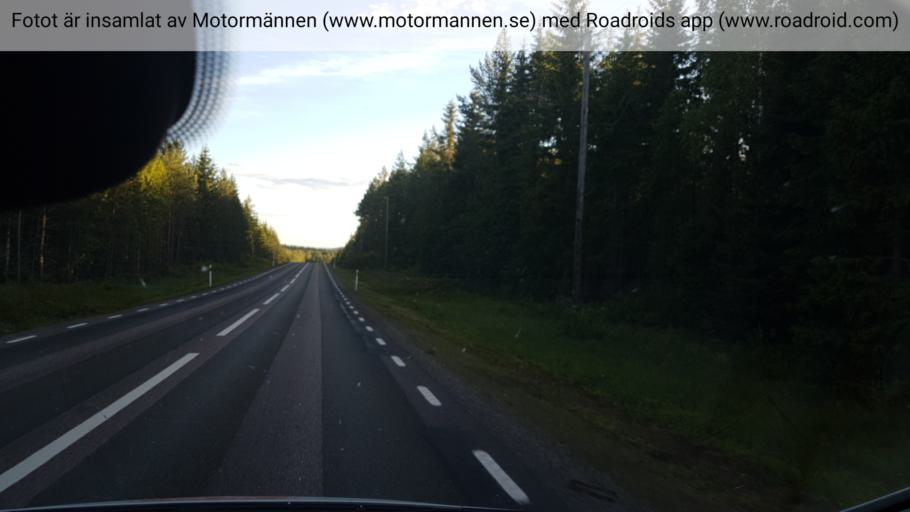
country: SE
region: Vaermland
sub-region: Torsby Kommun
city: Torsby
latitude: 60.2961
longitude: 13.0776
